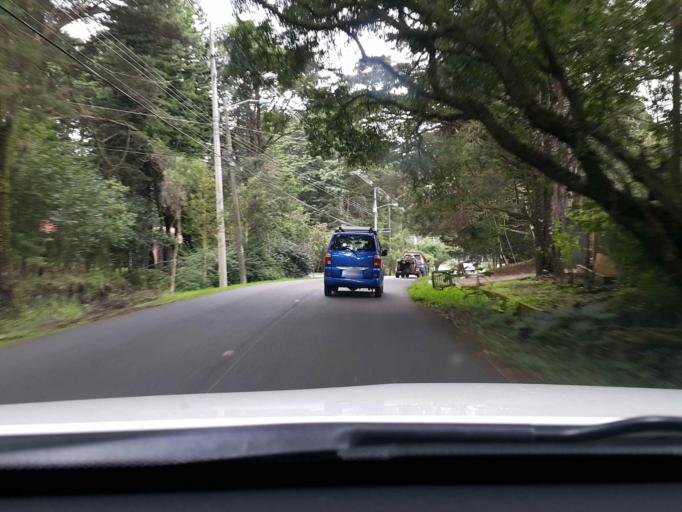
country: CR
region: Heredia
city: San Josecito
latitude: 10.0572
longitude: -84.0854
